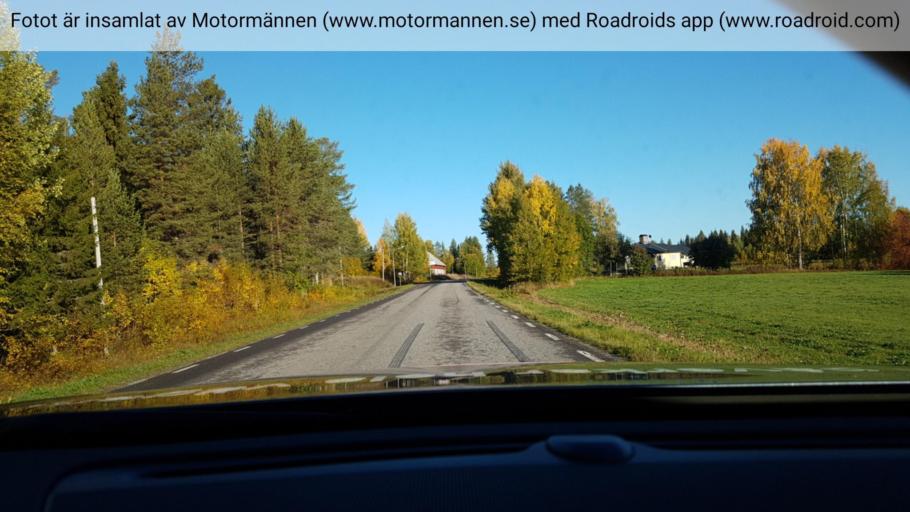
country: SE
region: Norrbotten
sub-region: Bodens Kommun
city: Boden
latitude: 65.9003
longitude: 21.6717
